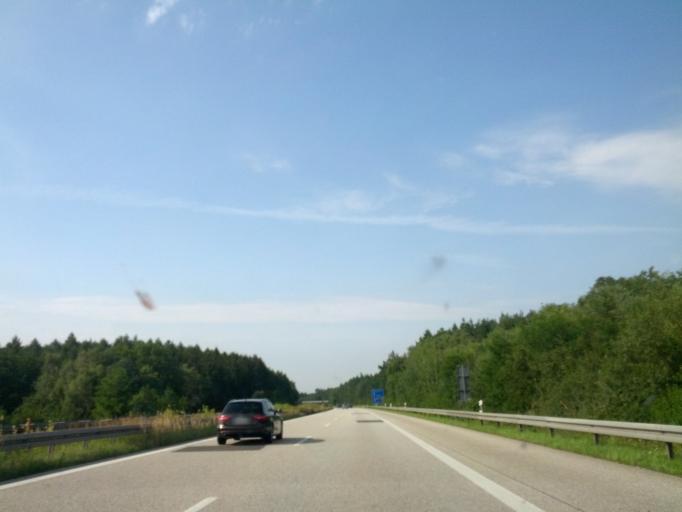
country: DE
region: Mecklenburg-Vorpommern
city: Lalendorf
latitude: 53.7654
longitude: 12.3248
